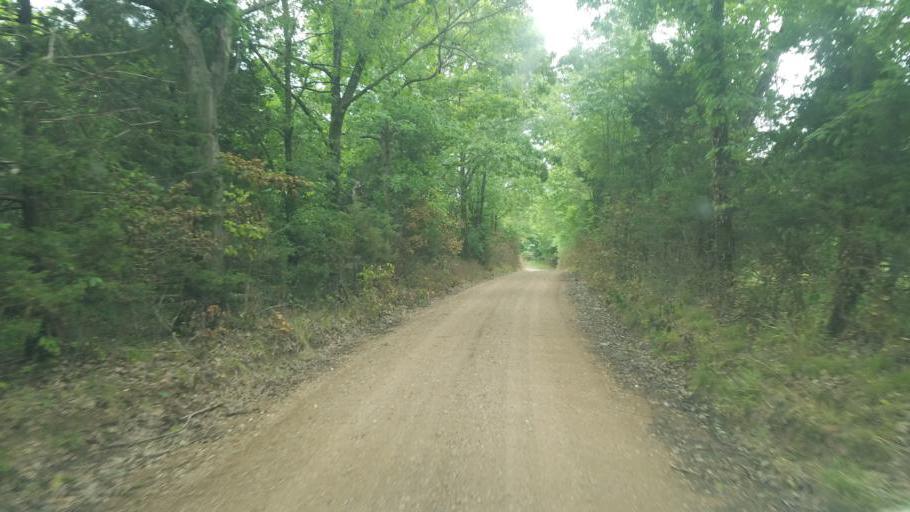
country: US
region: Missouri
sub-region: Moniteau County
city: California
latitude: 38.5911
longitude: -92.6518
